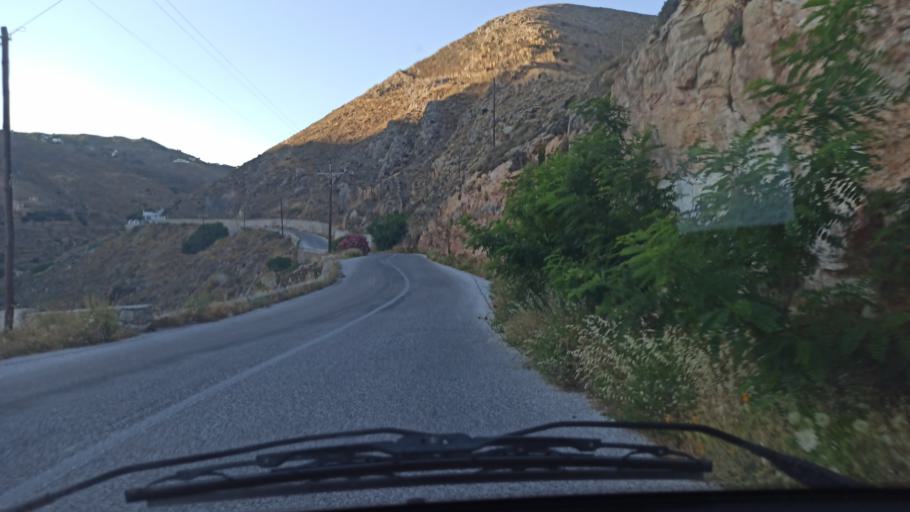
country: GR
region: South Aegean
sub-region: Nomos Kykladon
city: Ano Syros
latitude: 37.4541
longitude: 24.9336
